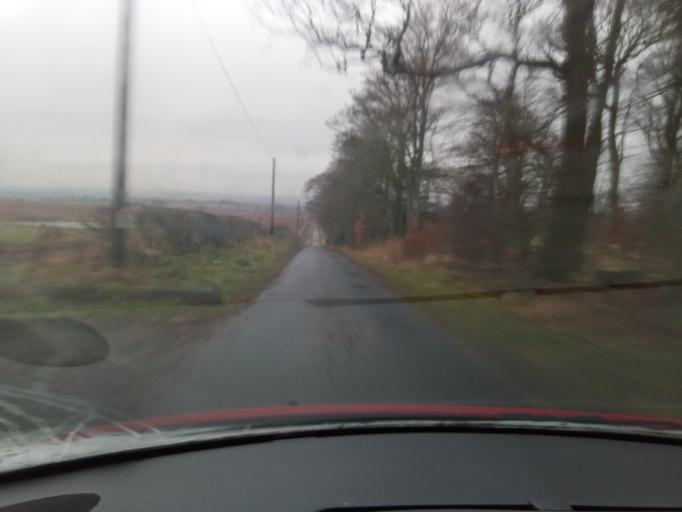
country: GB
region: Scotland
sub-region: The Scottish Borders
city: Kelso
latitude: 55.5607
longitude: -2.4273
